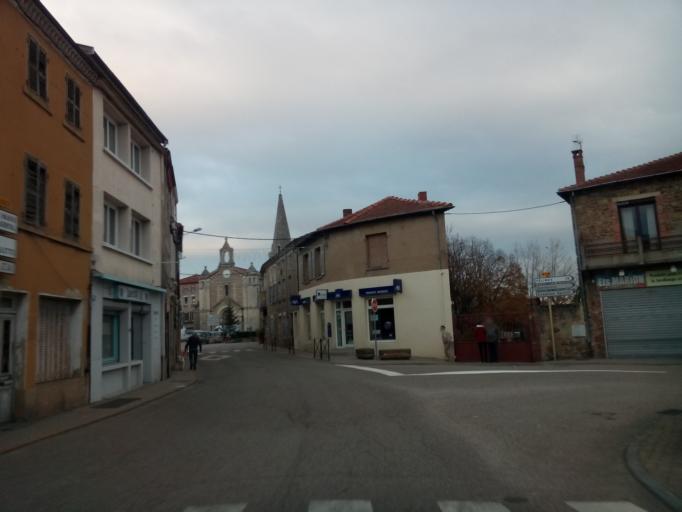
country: FR
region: Rhone-Alpes
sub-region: Departement de la Loire
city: Maclas
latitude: 45.3620
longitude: 4.6847
